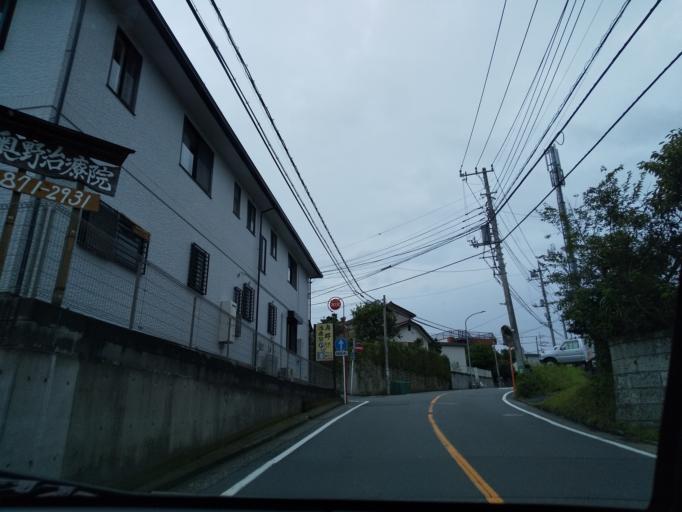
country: JP
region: Kanagawa
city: Fujisawa
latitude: 35.3922
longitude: 139.5068
